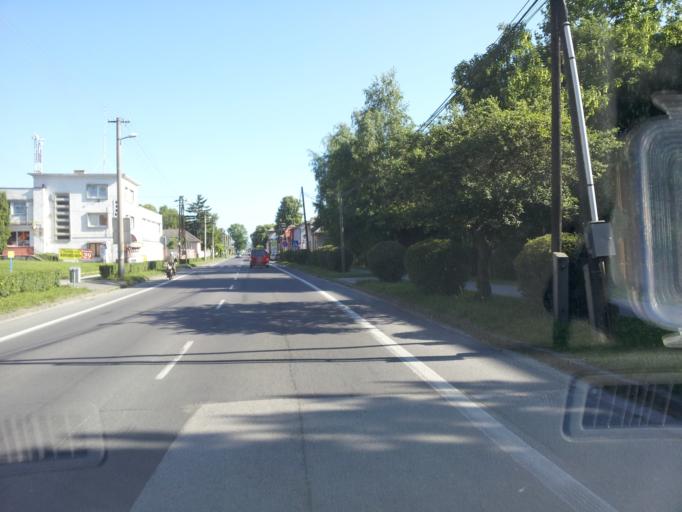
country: SK
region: Nitriansky
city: Sahy
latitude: 48.0735
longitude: 18.9469
